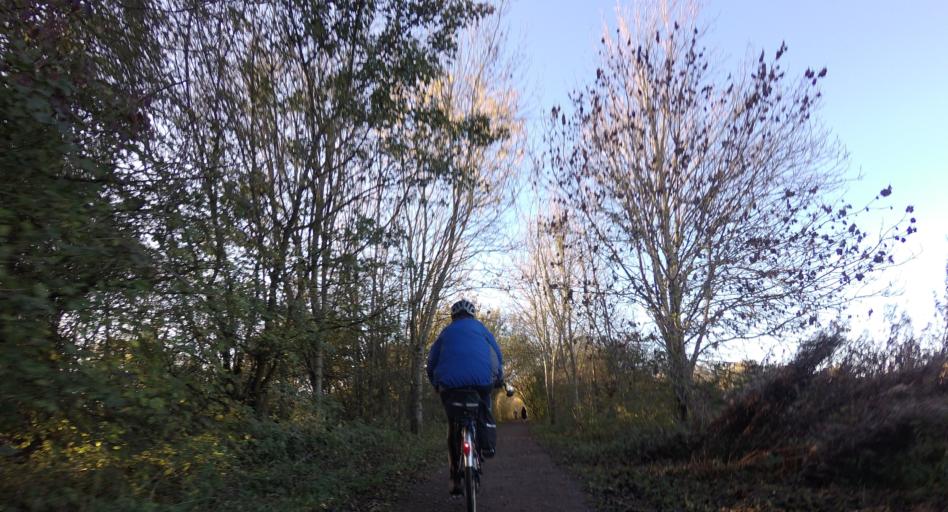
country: GB
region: England
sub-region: West Sussex
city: Steyning
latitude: 50.8797
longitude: -0.3127
